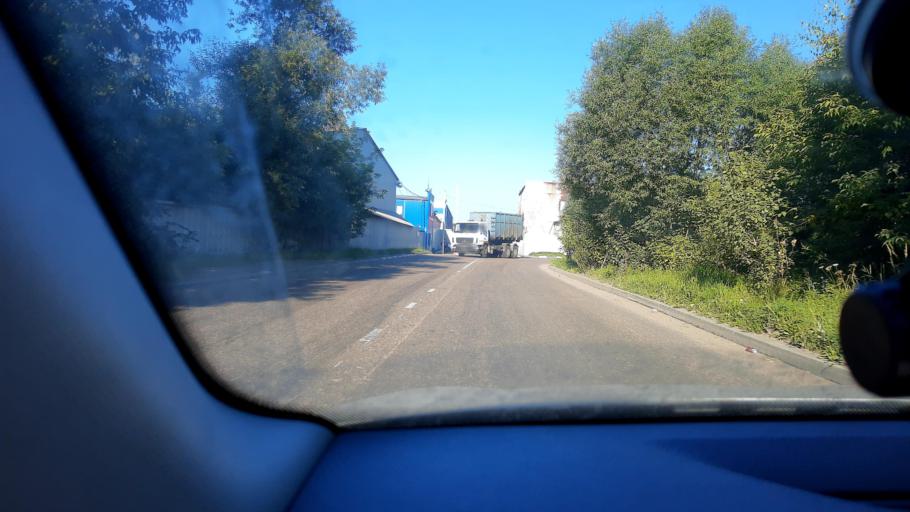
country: RU
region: Moskovskaya
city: Shcherbinka
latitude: 55.4643
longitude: 37.5701
